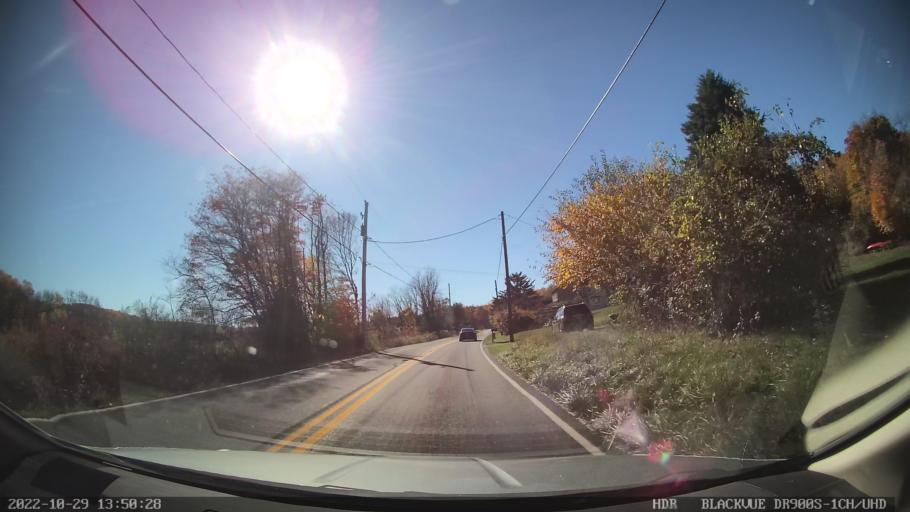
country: US
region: Pennsylvania
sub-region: Lehigh County
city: Emmaus
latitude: 40.5346
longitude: -75.4606
